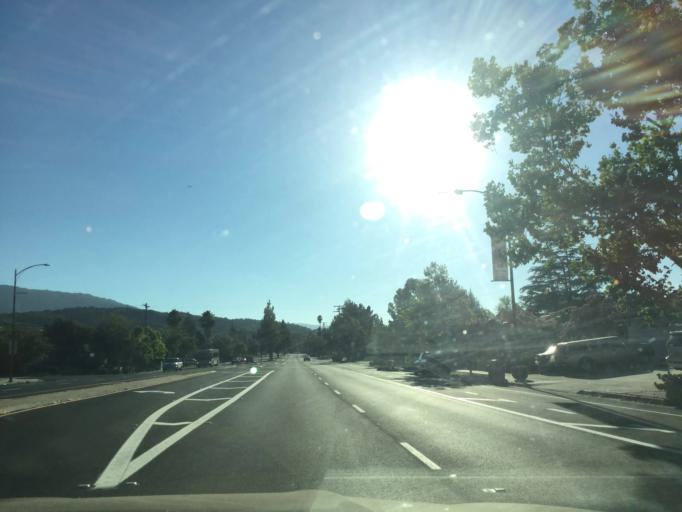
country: US
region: California
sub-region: Santa Clara County
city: Cambrian Park
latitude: 37.2222
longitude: -121.8707
